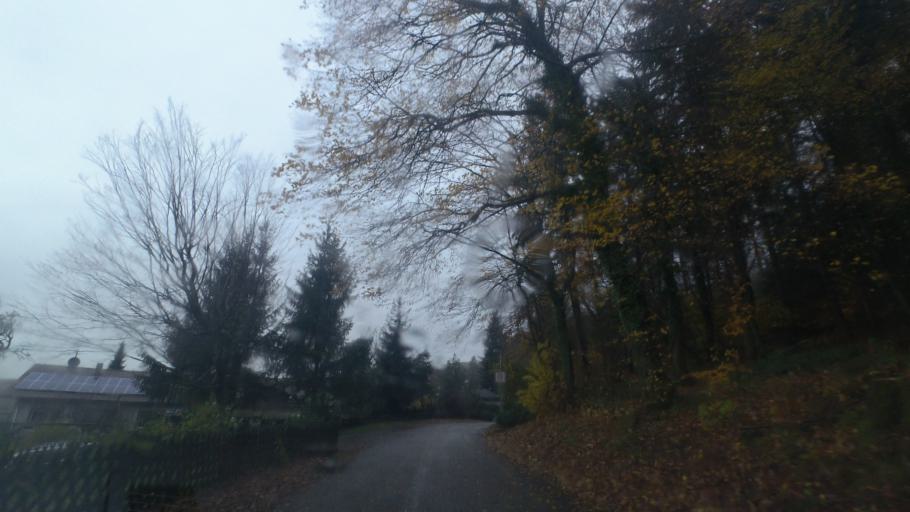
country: DE
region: Baden-Wuerttemberg
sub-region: Karlsruhe Region
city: Sinzheim
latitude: 48.7535
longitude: 8.1831
